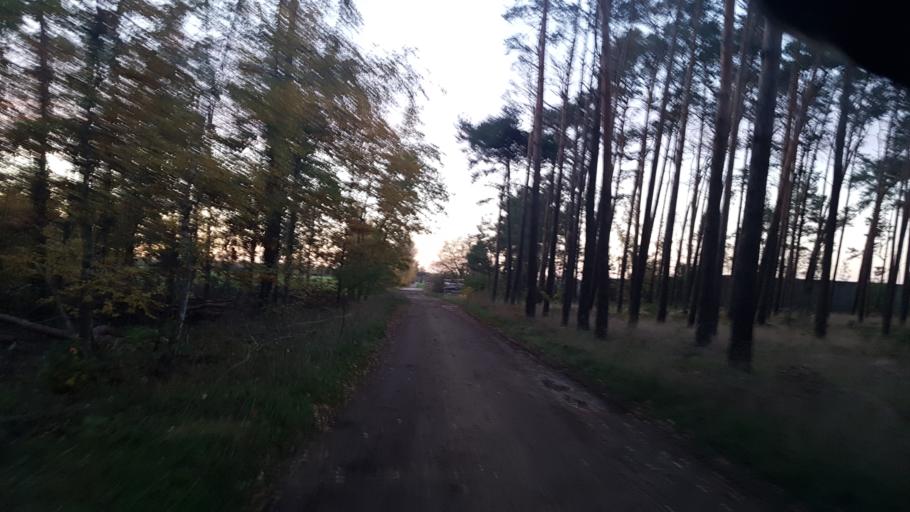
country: DE
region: Brandenburg
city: Bad Liebenwerda
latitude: 51.5087
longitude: 13.3173
